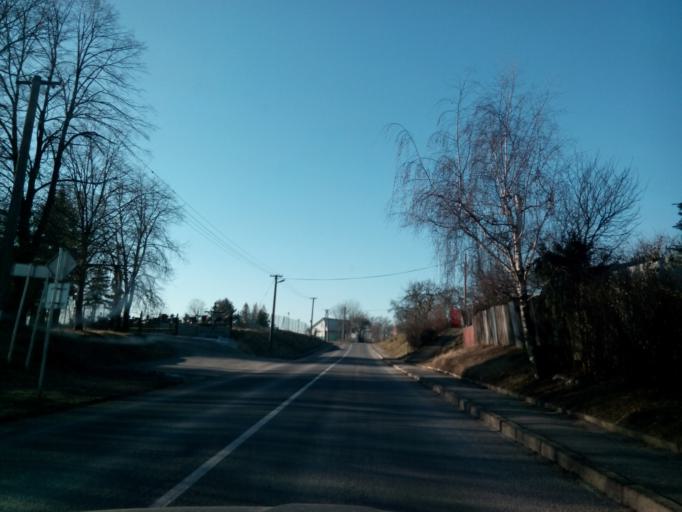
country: SK
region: Kosicky
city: Moldava nad Bodvou
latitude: 48.6887
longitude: 21.0089
